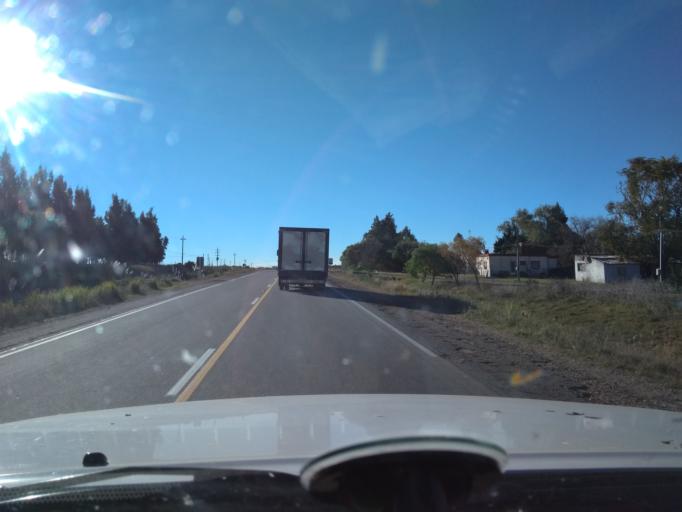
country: UY
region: Canelones
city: Sauce
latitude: -34.5909
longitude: -56.0530
